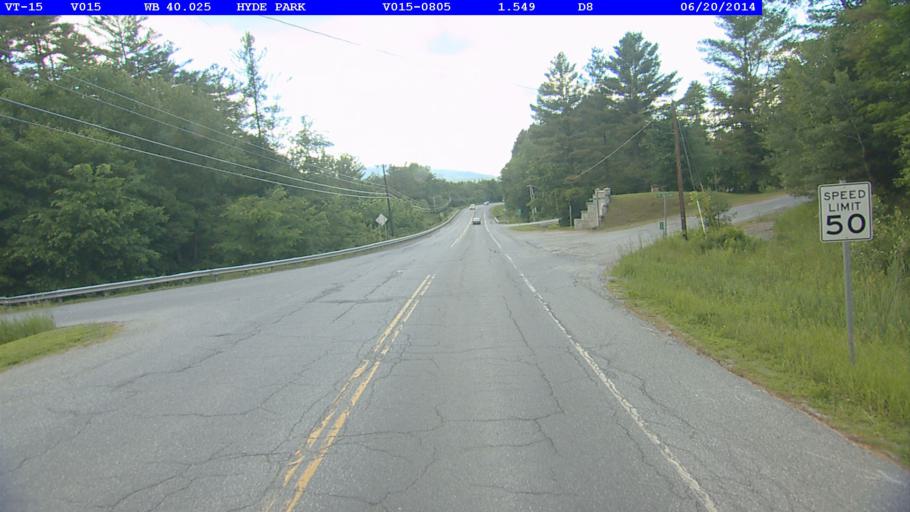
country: US
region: Vermont
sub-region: Lamoille County
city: Hyde Park
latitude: 44.5976
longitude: -72.6216
